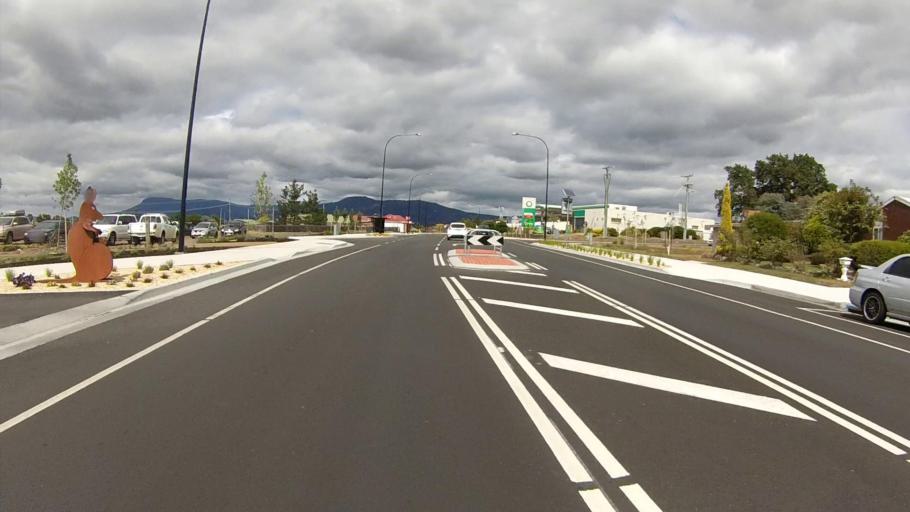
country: AU
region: Tasmania
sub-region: Brighton
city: Bridgewater
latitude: -42.6984
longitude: 147.2525
